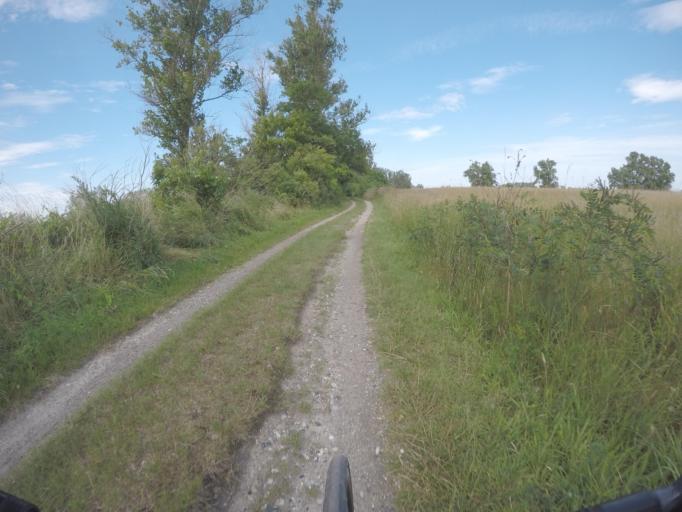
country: DE
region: Mecklenburg-Vorpommern
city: Altefahr
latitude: 54.3644
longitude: 13.1239
